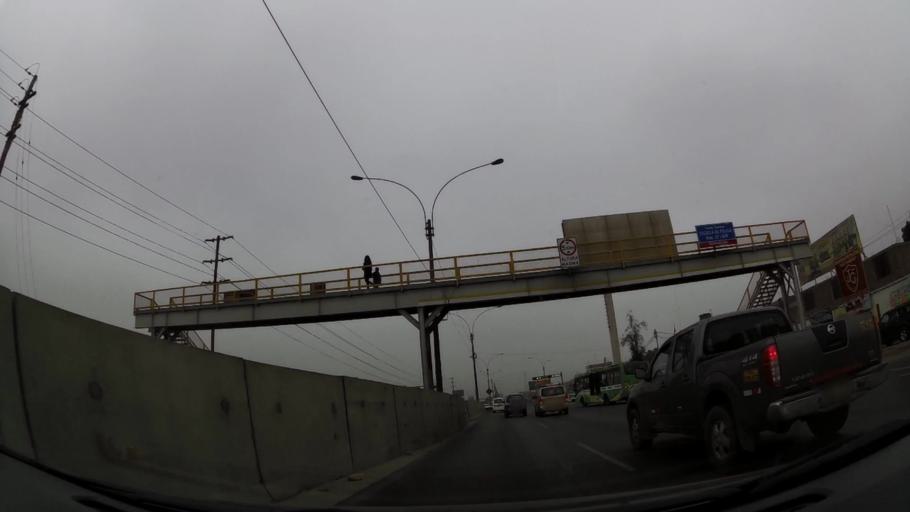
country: PE
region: Lima
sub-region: Lima
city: Urb. Santo Domingo
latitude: -11.8951
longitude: -77.0681
